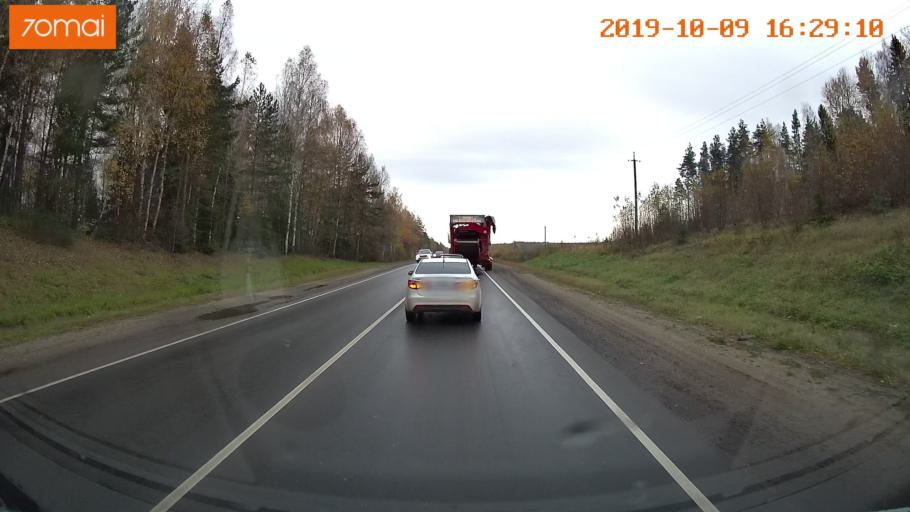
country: RU
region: Kostroma
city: Oktyabr'skiy
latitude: 57.6251
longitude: 40.9351
